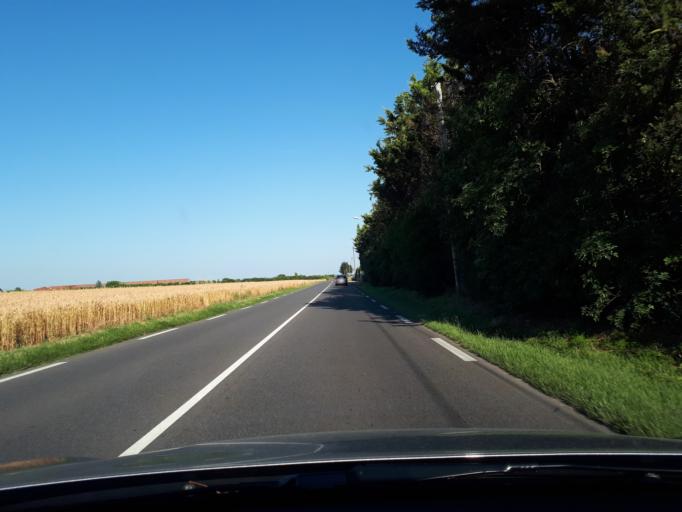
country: FR
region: Rhone-Alpes
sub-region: Departement du Rhone
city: Saint-Bonnet-de-Mure
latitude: 45.7257
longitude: 5.0340
